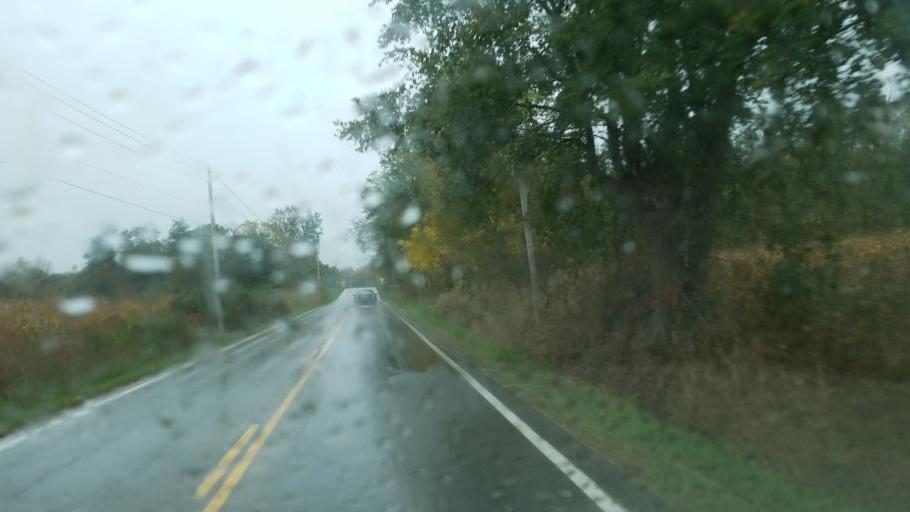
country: US
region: Ohio
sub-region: Richland County
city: Lincoln Heights
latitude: 40.8331
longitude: -82.4772
